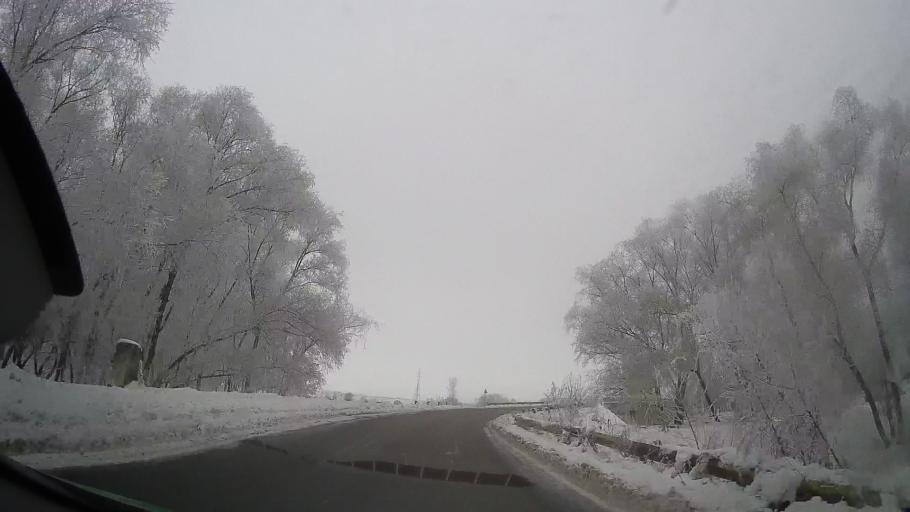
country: RO
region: Neamt
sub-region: Comuna Horia
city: Cotu Vames
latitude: 46.8813
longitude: 26.9721
